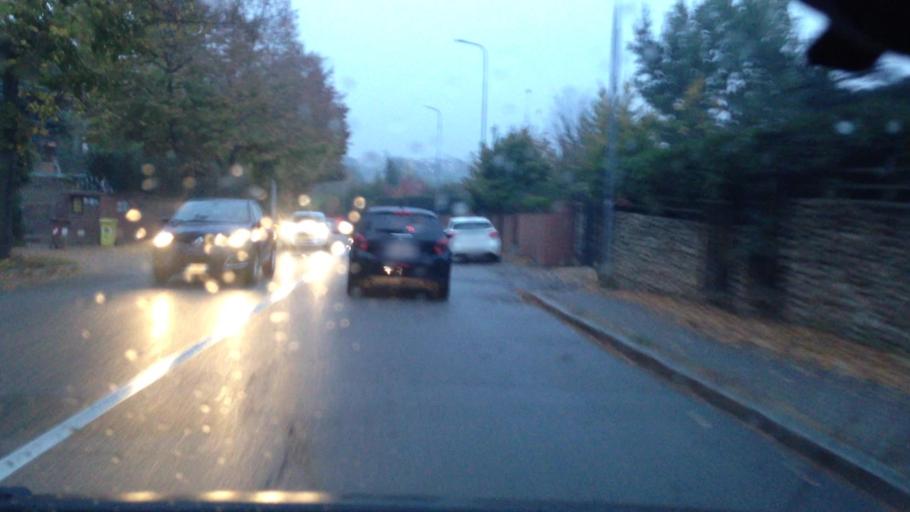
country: IT
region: Piedmont
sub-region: Provincia di Asti
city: Asti
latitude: 44.9133
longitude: 8.2073
